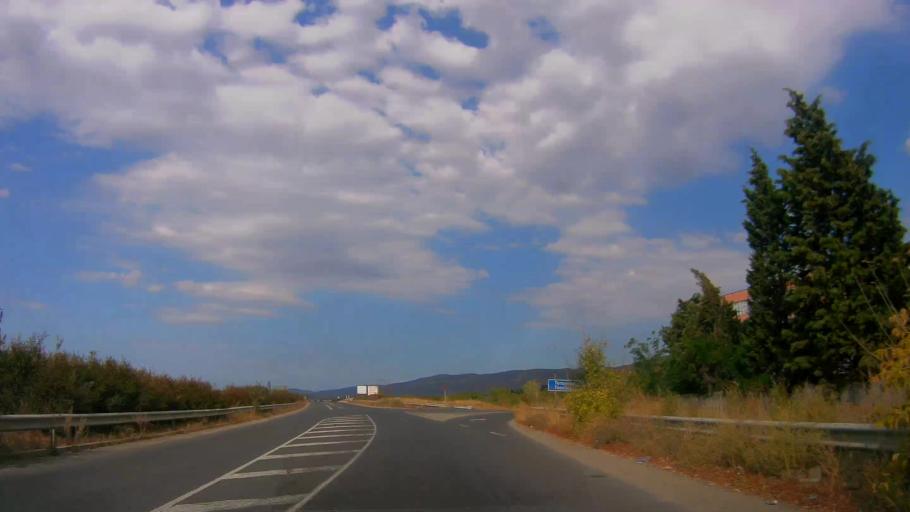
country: BG
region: Burgas
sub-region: Obshtina Aytos
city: Aytos
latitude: 42.7035
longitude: 27.2436
